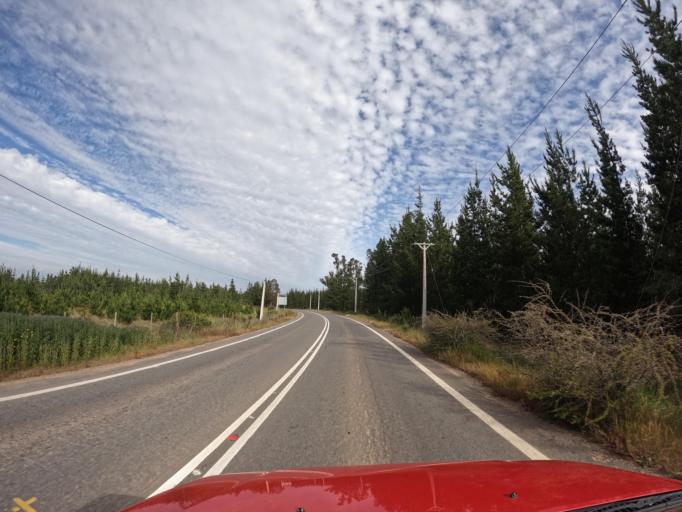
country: CL
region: O'Higgins
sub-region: Provincia de Colchagua
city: Santa Cruz
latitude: -34.3095
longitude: -71.8479
